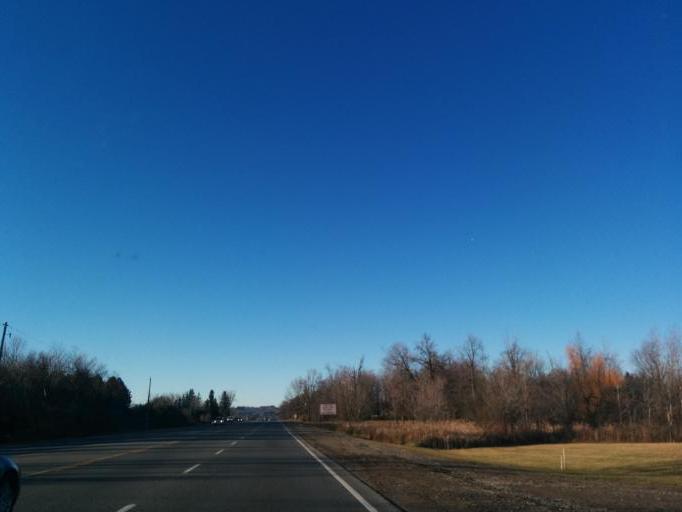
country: CA
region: Ontario
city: Brampton
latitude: 43.8024
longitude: -79.9175
